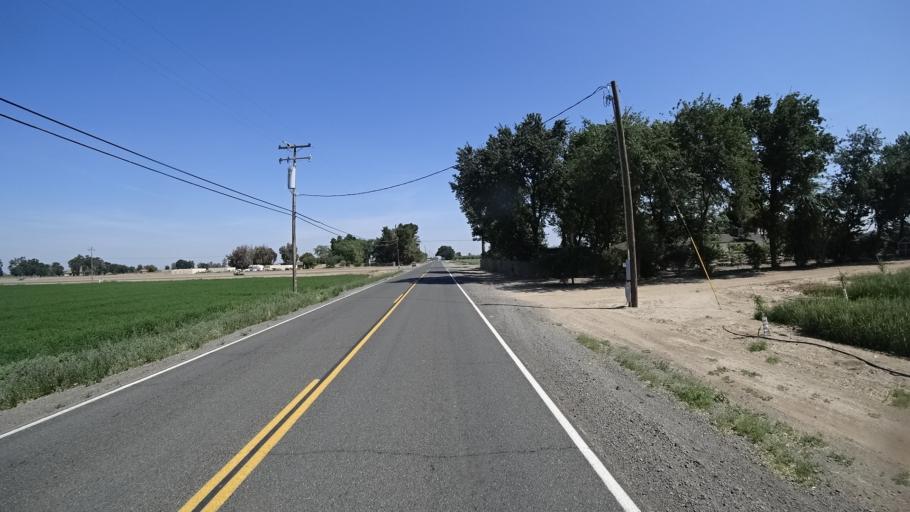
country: US
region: California
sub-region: Fresno County
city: Riverdale
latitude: 36.3577
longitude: -119.8513
